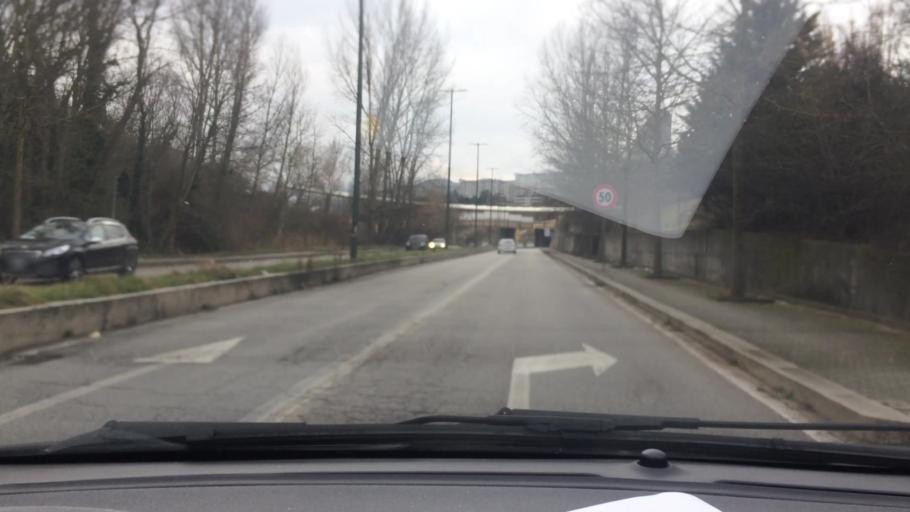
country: IT
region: Basilicate
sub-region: Provincia di Potenza
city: Potenza
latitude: 40.6389
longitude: 15.7965
